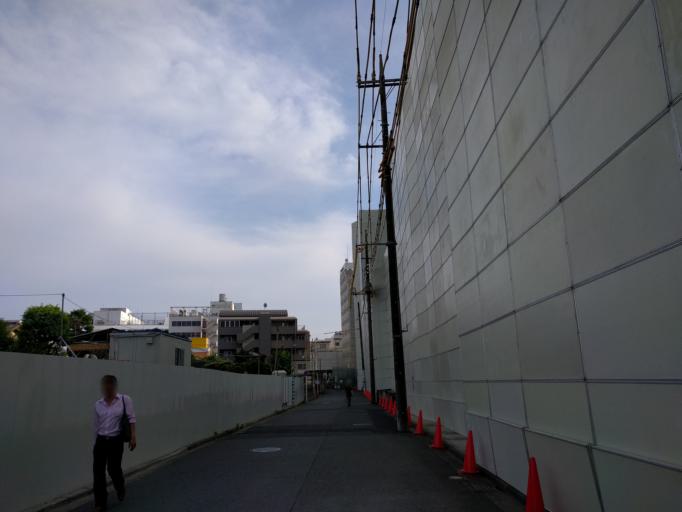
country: JP
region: Kanagawa
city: Kamakura
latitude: 35.3557
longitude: 139.5339
